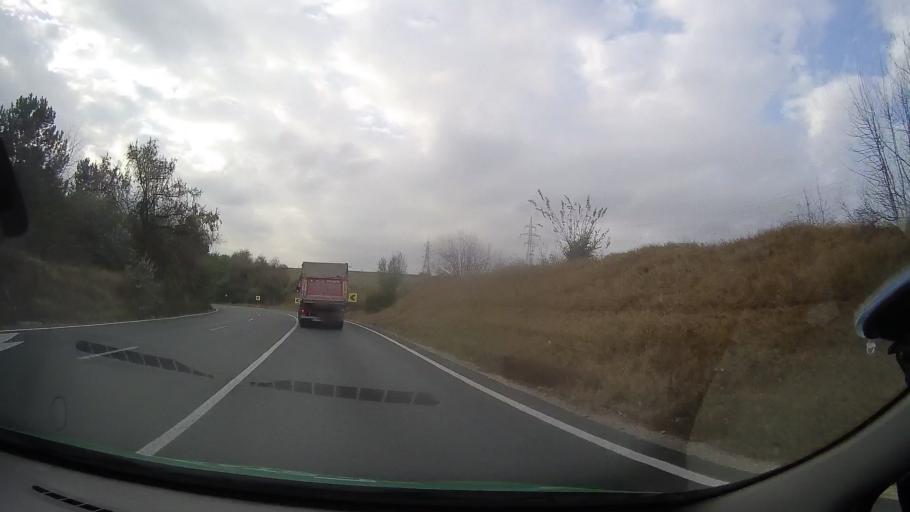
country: RO
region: Constanta
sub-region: Comuna Mircea Voda
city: Satu Nou
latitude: 44.2711
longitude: 28.1962
